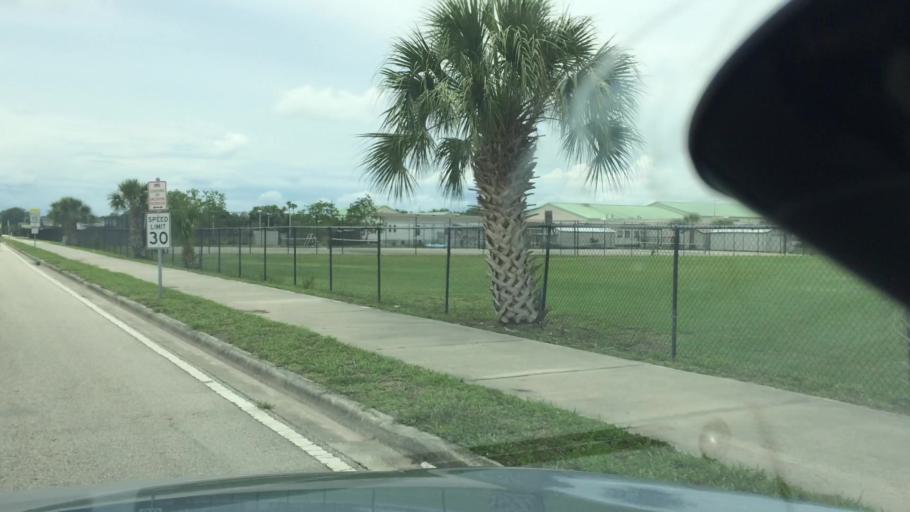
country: US
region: Florida
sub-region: Osceola County
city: Kissimmee
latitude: 28.3190
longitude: -81.4367
